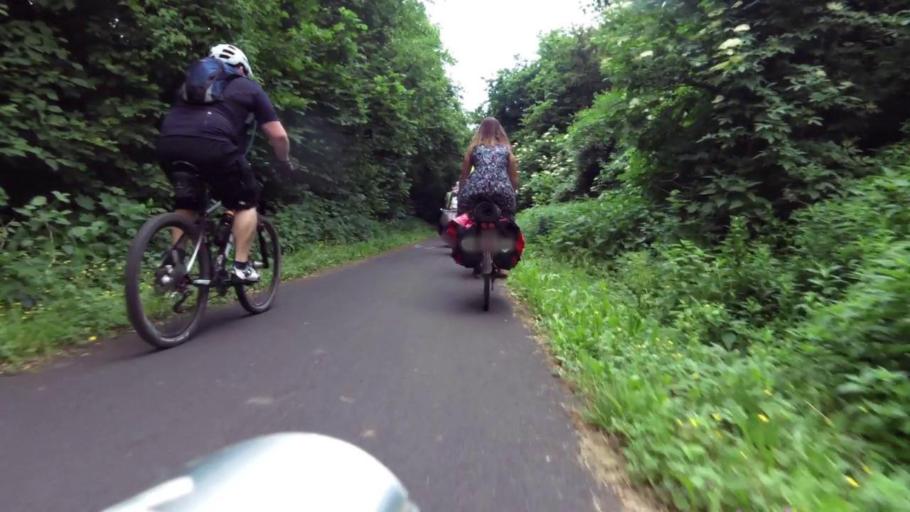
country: PL
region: Kujawsko-Pomorskie
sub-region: Powiat torunski
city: Lubianka
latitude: 53.0904
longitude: 18.5332
